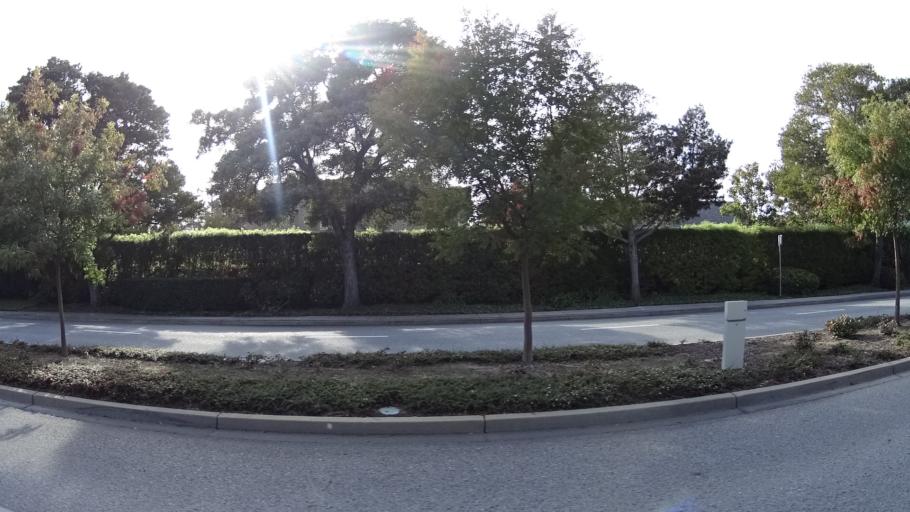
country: US
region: California
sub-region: San Mateo County
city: Redwood Shores
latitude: 37.5373
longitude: -122.2662
